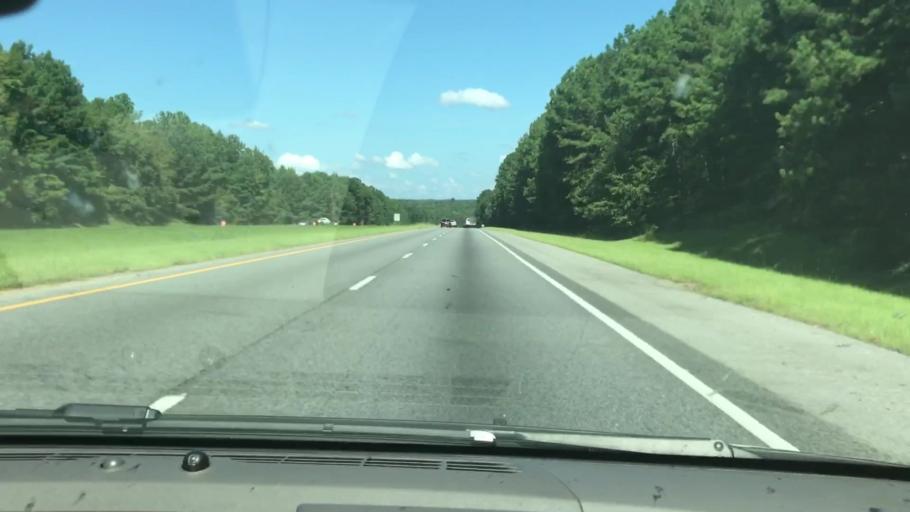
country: US
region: Georgia
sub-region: Harris County
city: Hamilton
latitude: 32.6287
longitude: -84.9594
